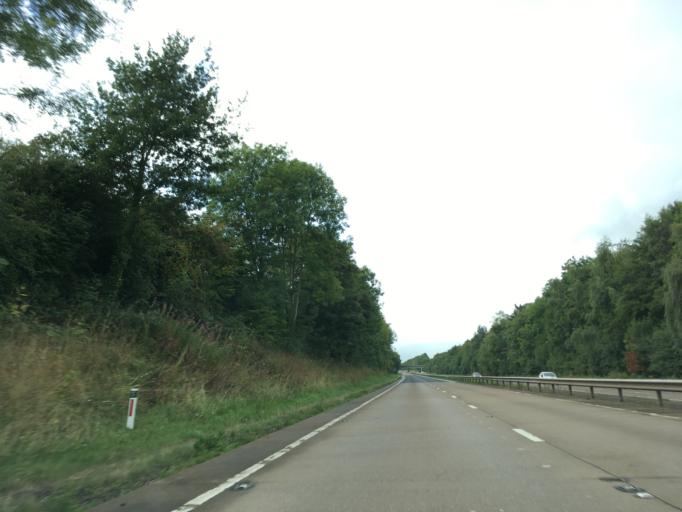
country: GB
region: Wales
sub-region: Monmouthshire
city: Llanarth
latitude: 51.7815
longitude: -2.9168
